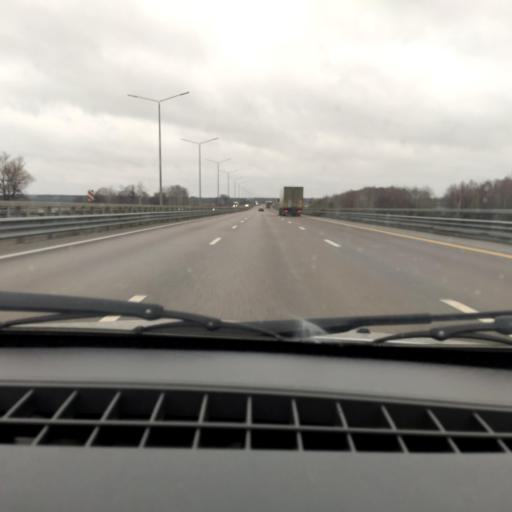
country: RU
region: Voronezj
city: Somovo
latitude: 51.7914
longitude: 39.2714
